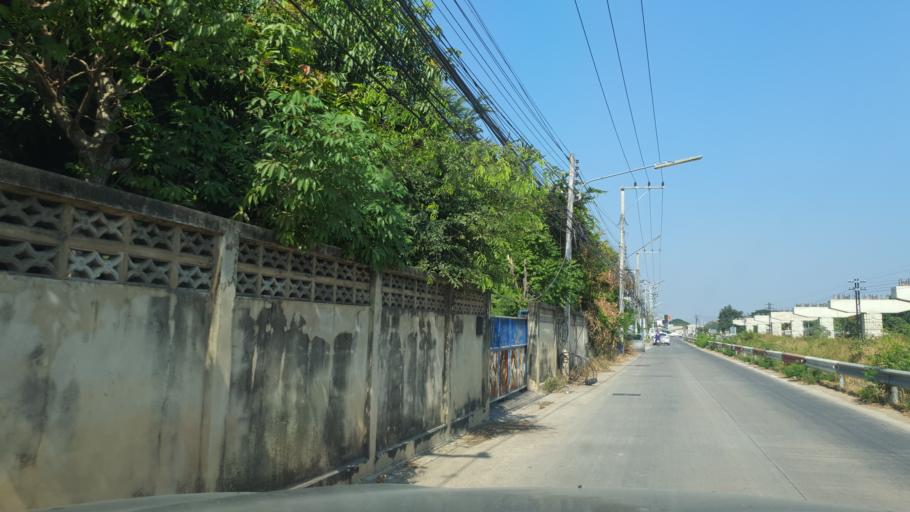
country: TH
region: Prachuap Khiri Khan
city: Hua Hin
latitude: 12.5587
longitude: 99.9565
